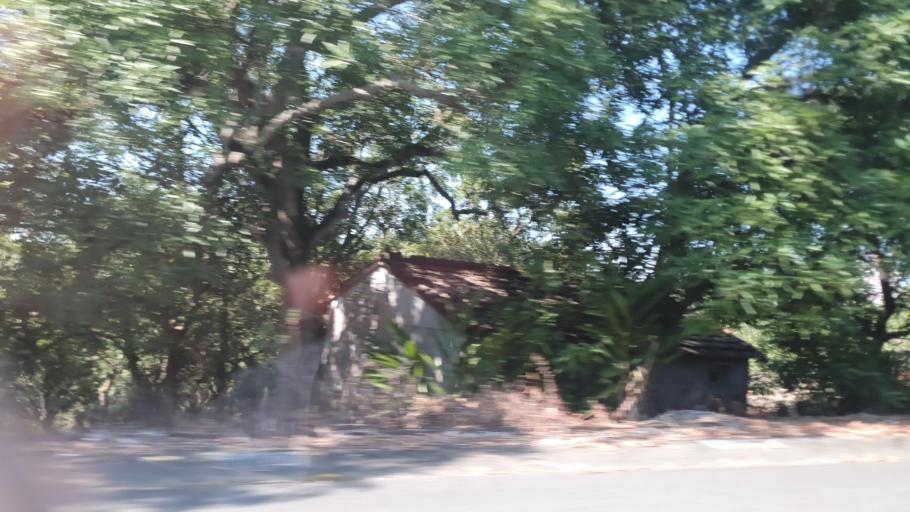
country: TW
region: Taiwan
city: Yujing
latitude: 23.0364
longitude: 120.3581
